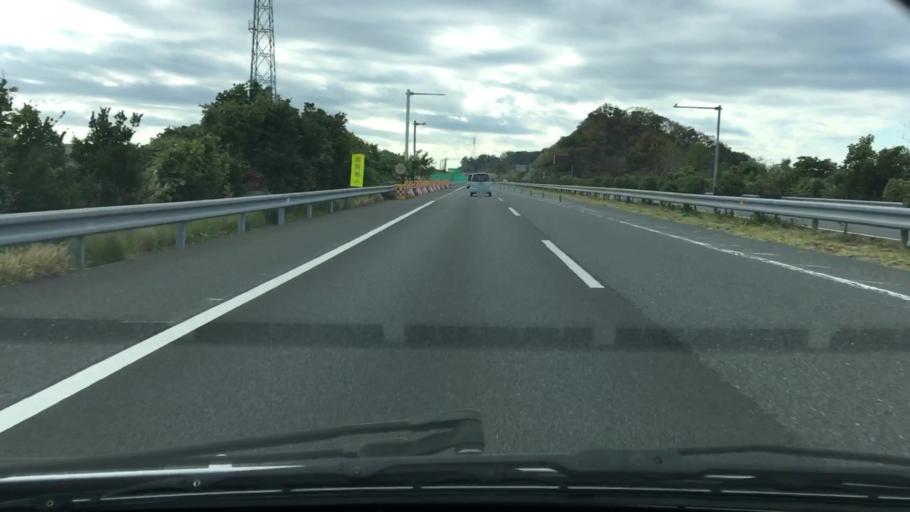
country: JP
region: Chiba
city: Kimitsu
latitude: 35.2475
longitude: 139.8907
